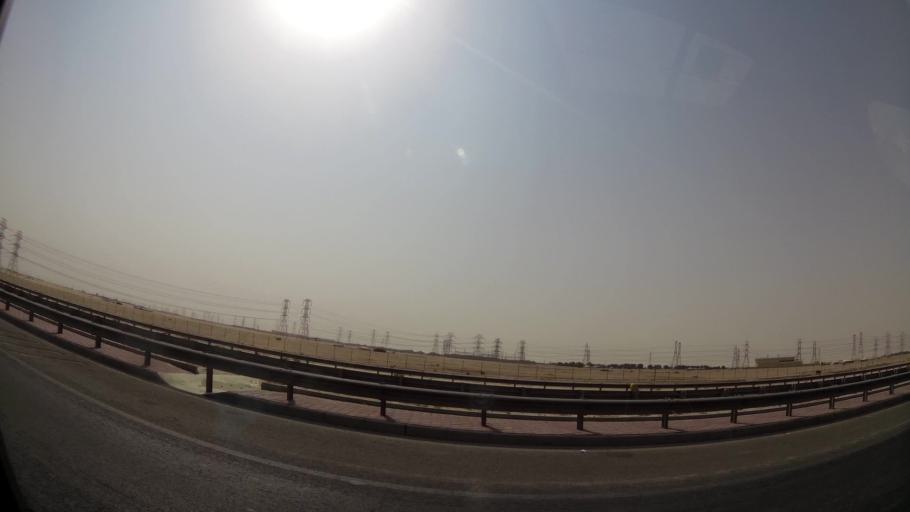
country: KW
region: Muhafazat al Jahra'
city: Al Jahra'
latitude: 29.2997
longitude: 47.7015
